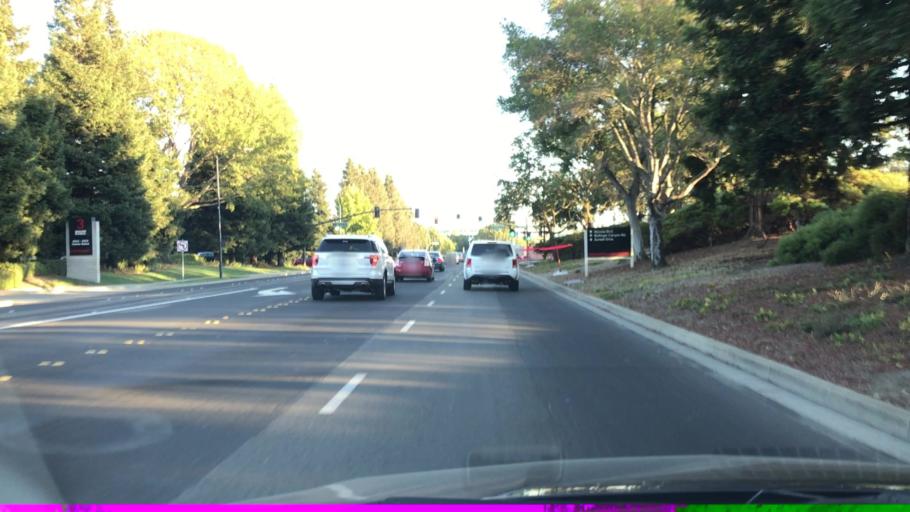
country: US
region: California
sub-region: Contra Costa County
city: San Ramon
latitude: 37.7655
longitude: -121.9591
